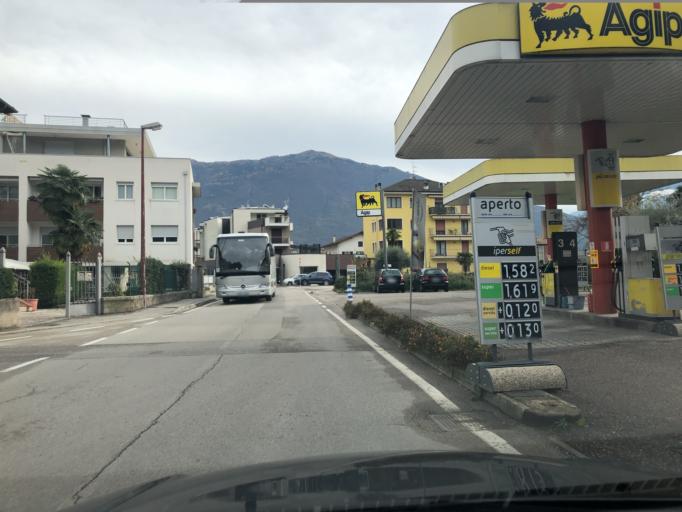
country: IT
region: Trentino-Alto Adige
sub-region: Provincia di Trento
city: Arco
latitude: 45.9180
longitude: 10.8676
